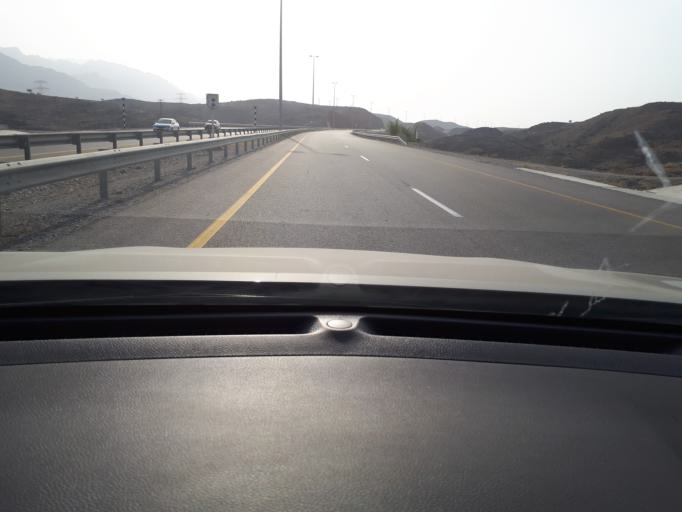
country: OM
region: Muhafazat Masqat
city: Muscat
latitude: 23.1936
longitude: 58.8372
